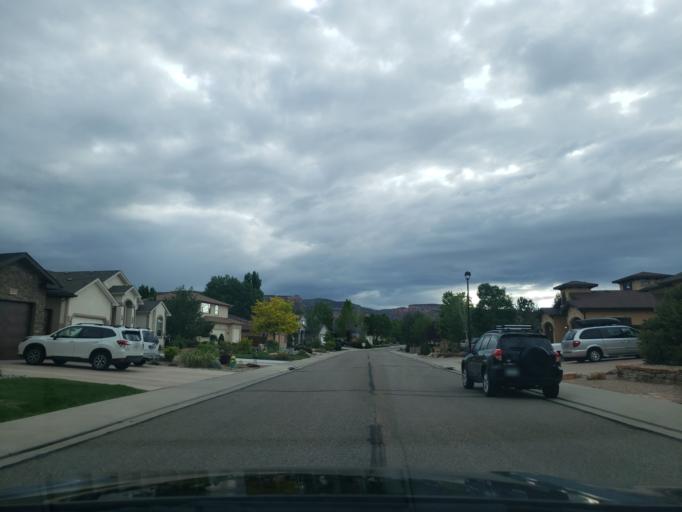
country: US
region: Colorado
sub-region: Mesa County
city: Redlands
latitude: 39.1061
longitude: -108.6661
